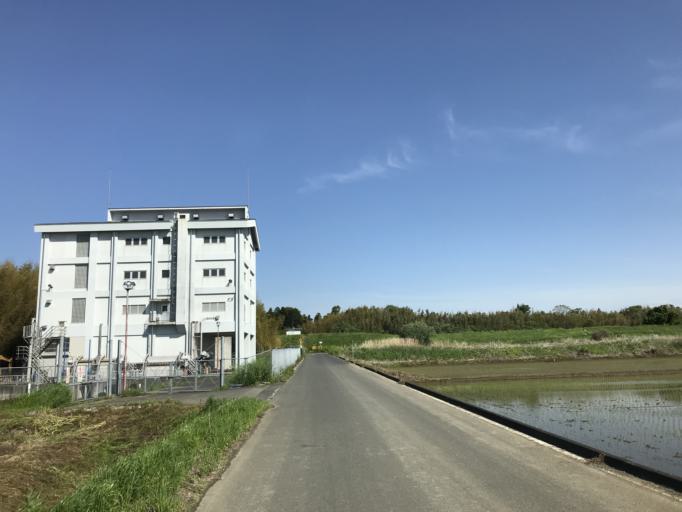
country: JP
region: Ibaraki
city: Moriya
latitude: 35.9658
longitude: 139.9483
